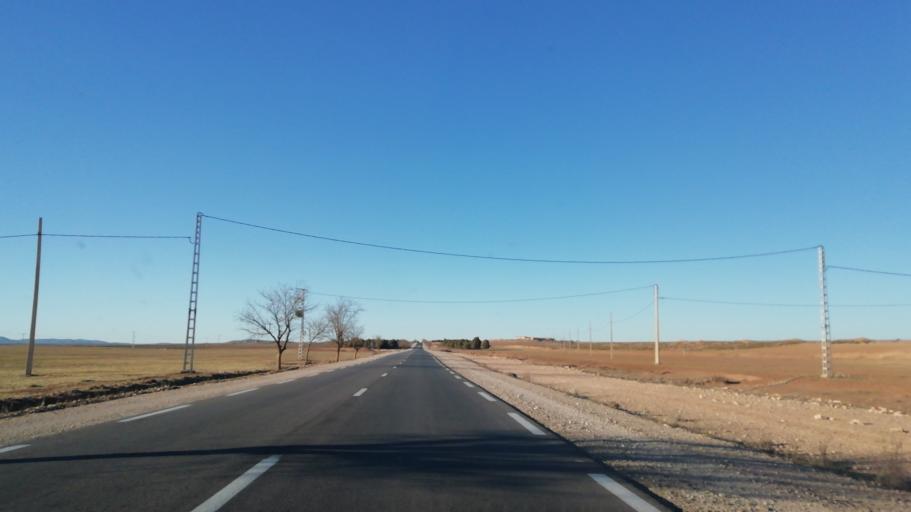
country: DZ
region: Tlemcen
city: Sebdou
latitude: 34.5211
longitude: -1.2893
